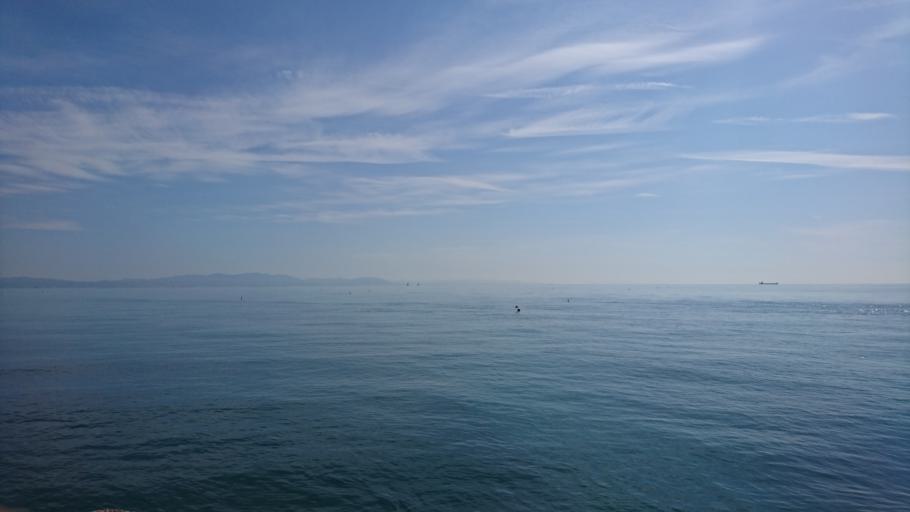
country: JP
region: Hyogo
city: Kakogawacho-honmachi
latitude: 34.6973
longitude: 134.8367
